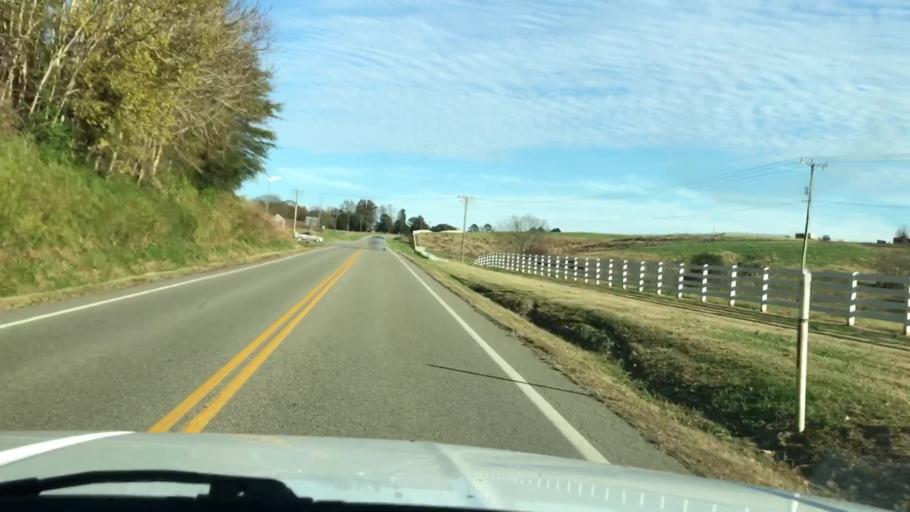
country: US
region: Virginia
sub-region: Goochland County
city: Goochland
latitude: 37.6472
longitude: -77.8245
